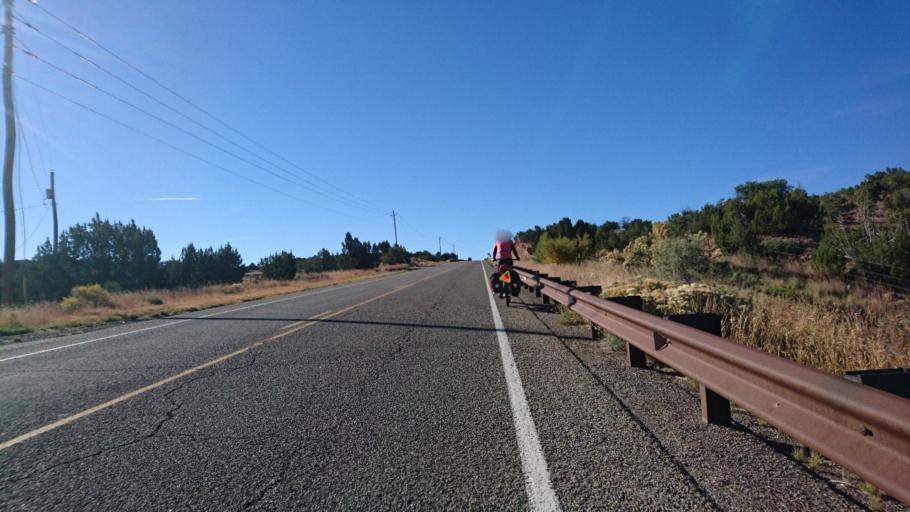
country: US
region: New Mexico
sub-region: Santa Fe County
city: La Cienega
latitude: 35.4571
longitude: -106.0700
